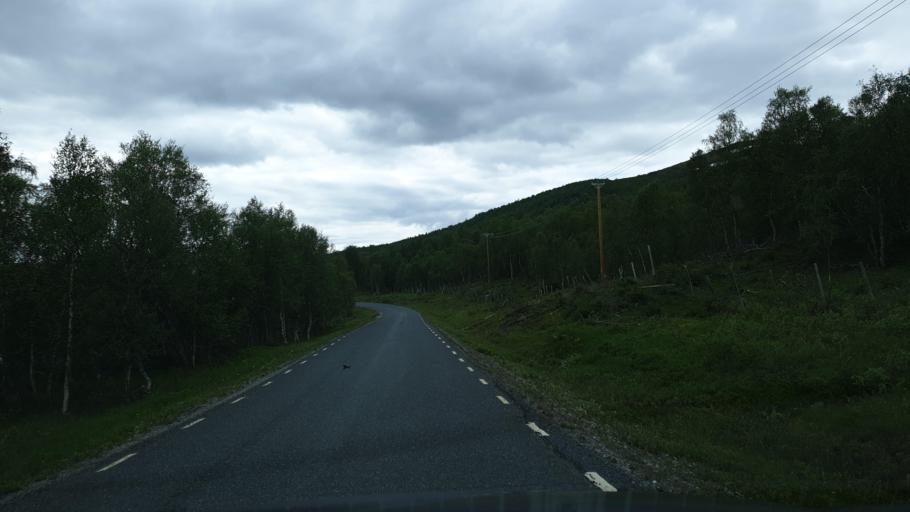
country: NO
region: Nordland
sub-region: Hattfjelldal
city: Hattfjelldal
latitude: 65.4177
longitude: 14.7841
